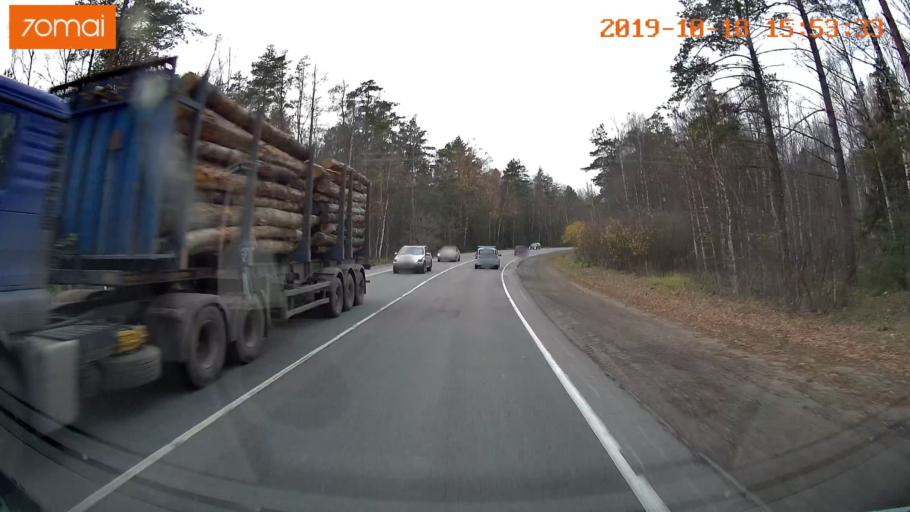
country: RU
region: Vladimir
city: Kommunar
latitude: 56.0557
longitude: 40.5201
